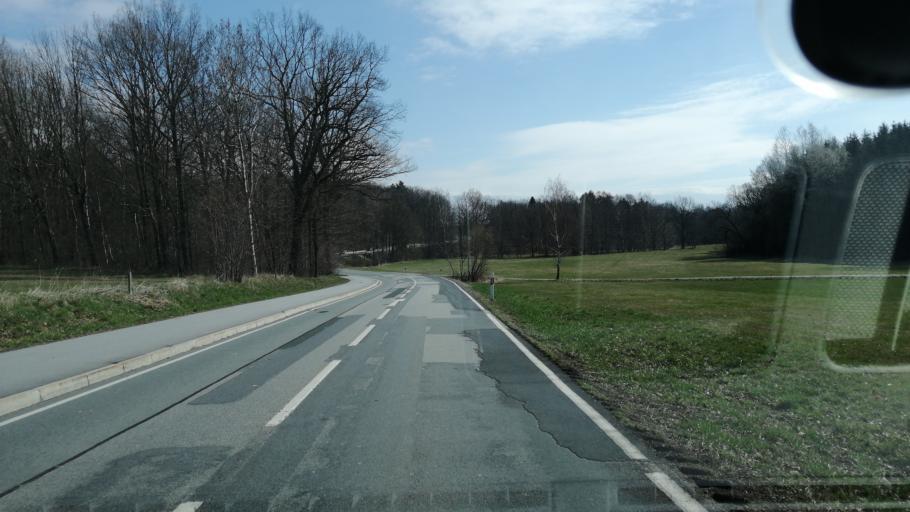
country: DE
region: Saxony
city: Grossschweidnitz
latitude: 51.0843
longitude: 14.6249
